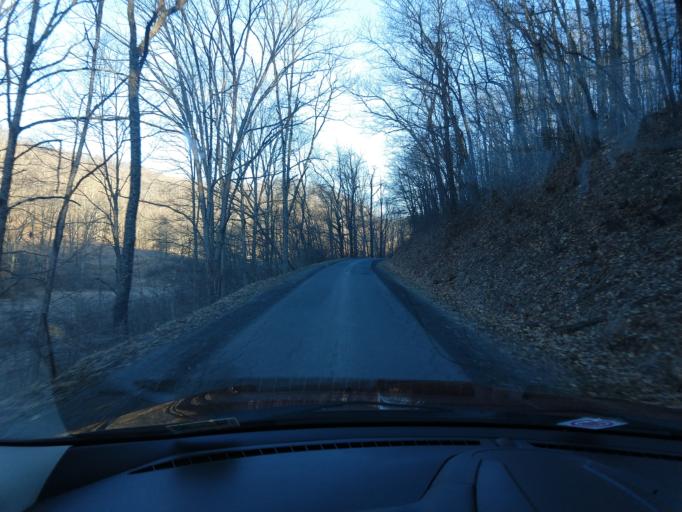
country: US
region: West Virginia
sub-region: Greenbrier County
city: Rainelle
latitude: 37.8918
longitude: -80.7308
